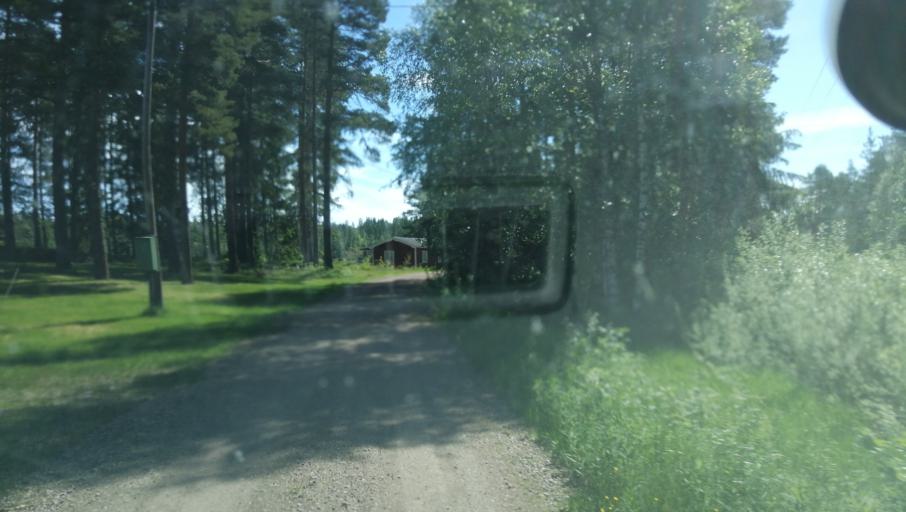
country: SE
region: Dalarna
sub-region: Vansbro Kommun
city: Vansbro
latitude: 60.8264
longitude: 14.1836
